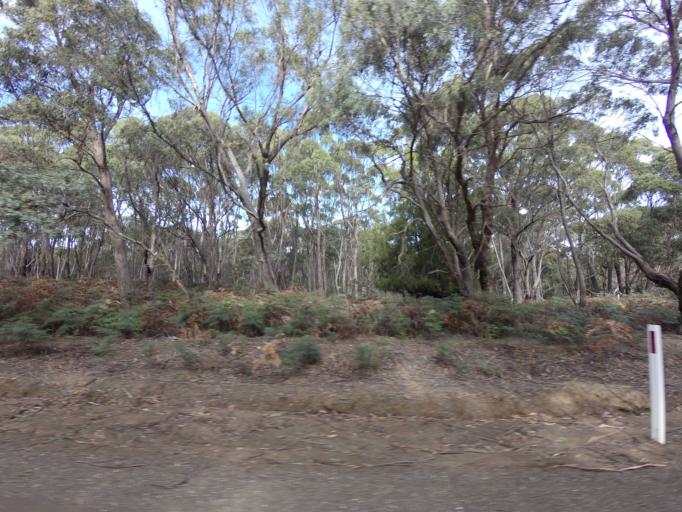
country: AU
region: Tasmania
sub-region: Clarence
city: Sandford
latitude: -43.0838
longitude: 147.6823
